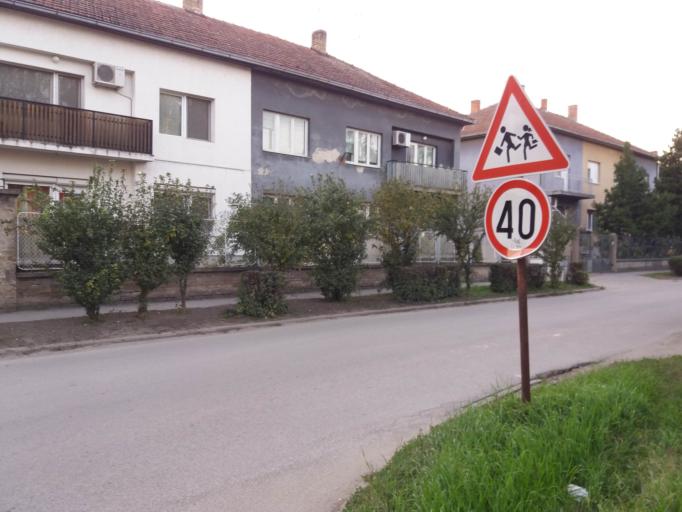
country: RS
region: Autonomna Pokrajina Vojvodina
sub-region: Severnobacki Okrug
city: Subotica
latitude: 46.1009
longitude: 19.6864
